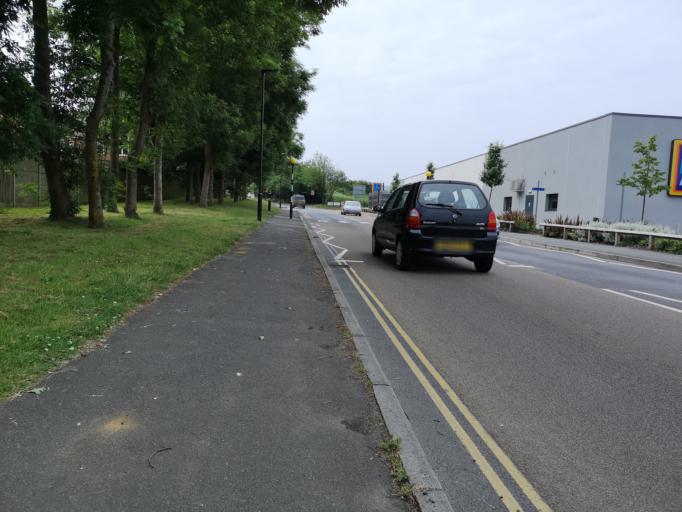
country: GB
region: England
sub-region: Isle of Wight
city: Sandown
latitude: 50.6458
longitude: -1.1788
